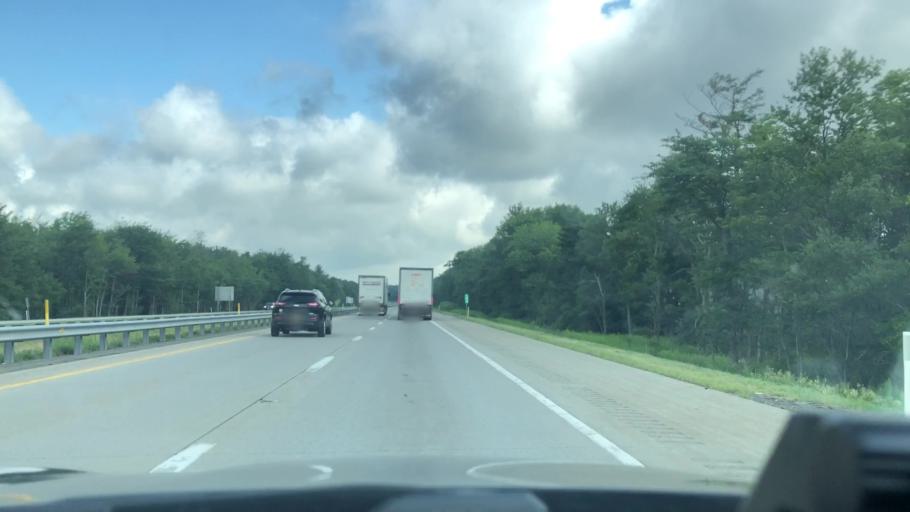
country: US
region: Pennsylvania
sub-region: Monroe County
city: Mount Pocono
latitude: 41.1309
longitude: -75.4005
